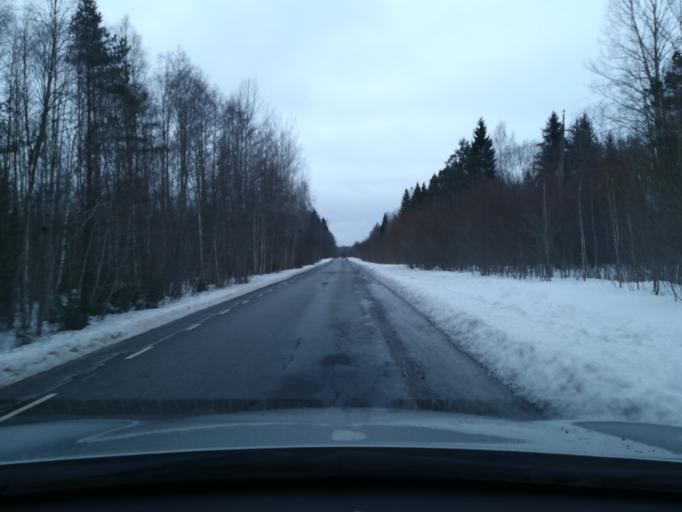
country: EE
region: Harju
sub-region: Nissi vald
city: Turba
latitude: 59.0664
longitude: 24.2524
